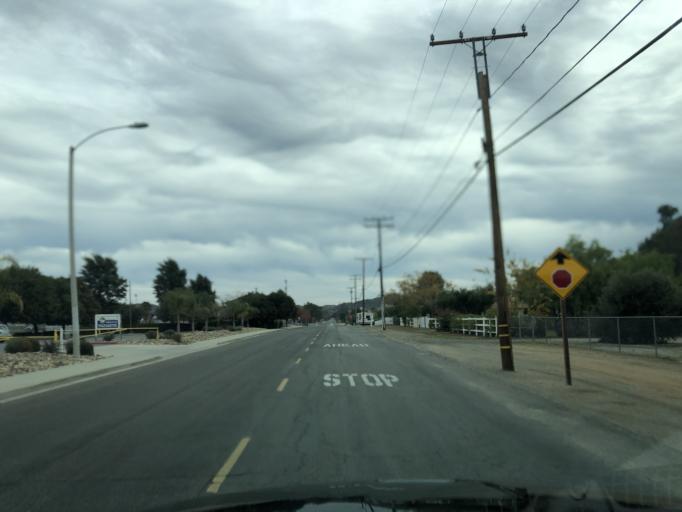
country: US
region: California
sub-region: Riverside County
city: Sedco Hills
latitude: 33.6232
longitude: -117.2862
